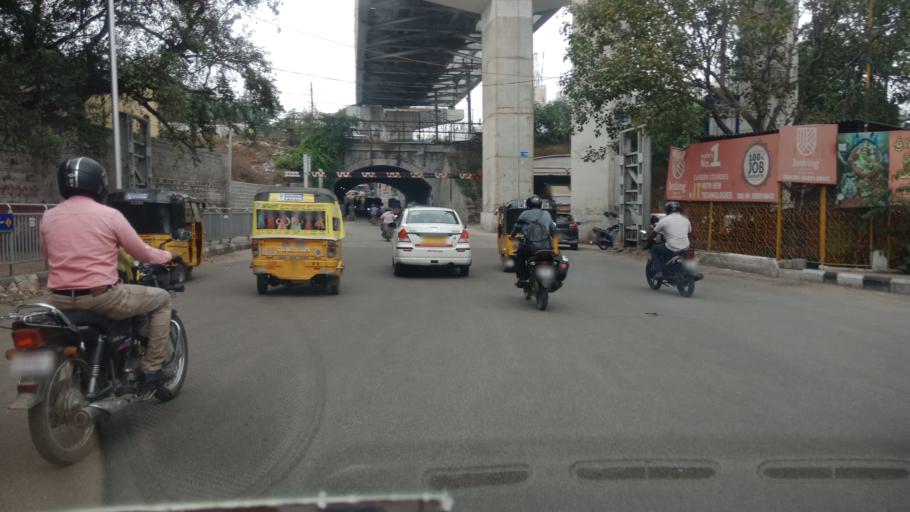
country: IN
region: Telangana
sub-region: Hyderabad
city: Malkajgiri
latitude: 17.4334
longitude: 78.5060
